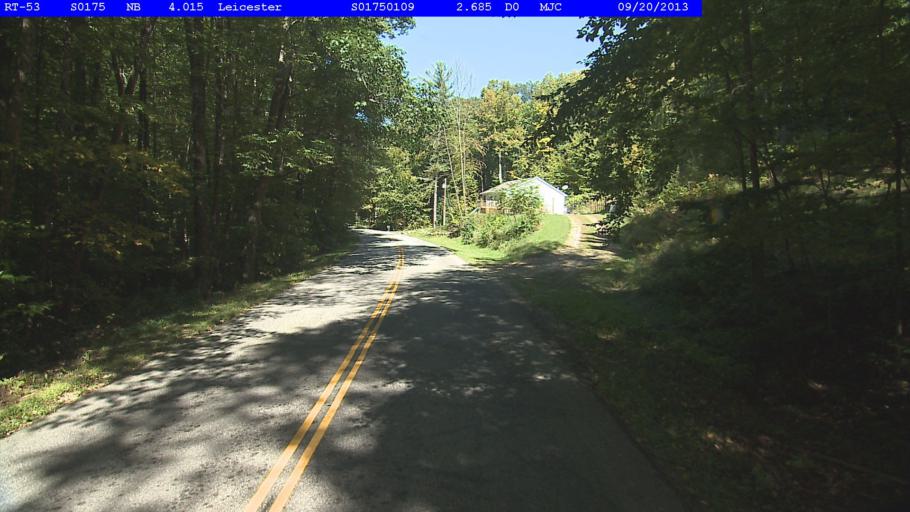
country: US
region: Vermont
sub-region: Rutland County
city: Brandon
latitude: 43.8814
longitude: -73.0635
